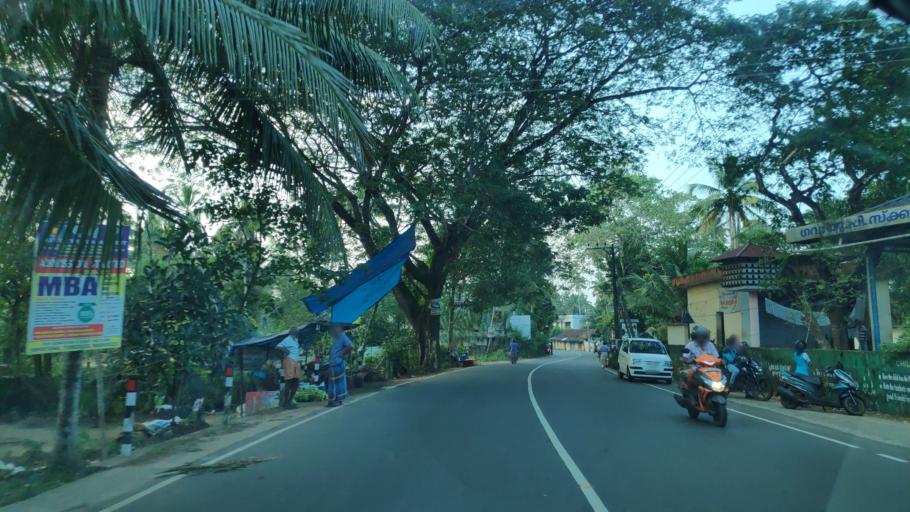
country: IN
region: Kerala
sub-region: Alappuzha
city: Shertallai
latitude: 9.6821
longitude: 76.3631
